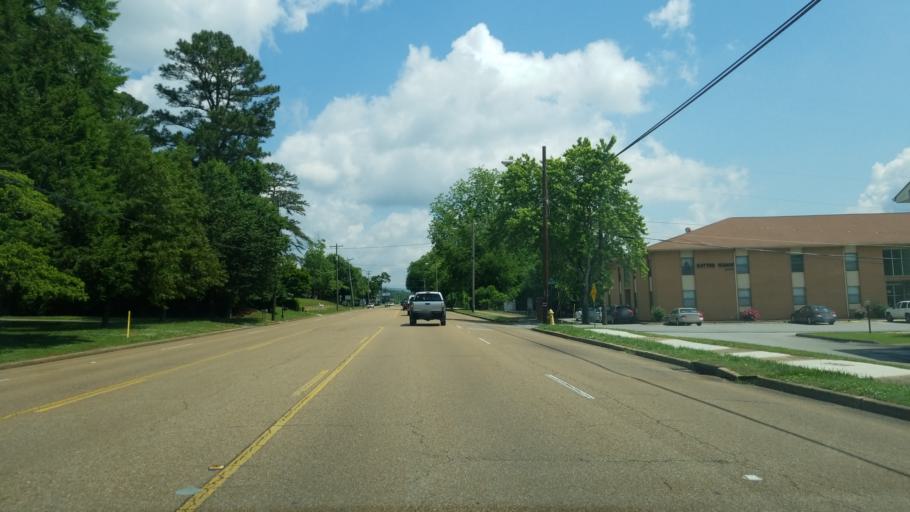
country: US
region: Tennessee
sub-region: Hamilton County
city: Red Bank
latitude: 35.1304
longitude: -85.2829
